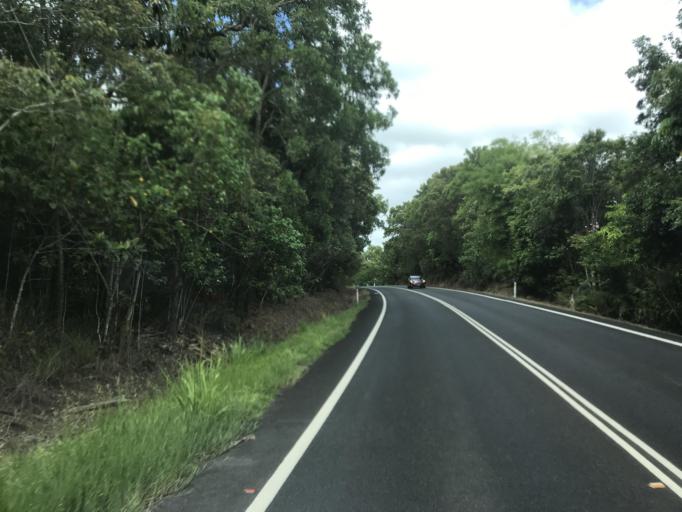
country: AU
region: Queensland
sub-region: Cassowary Coast
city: Innisfail
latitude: -17.8120
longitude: 146.0309
